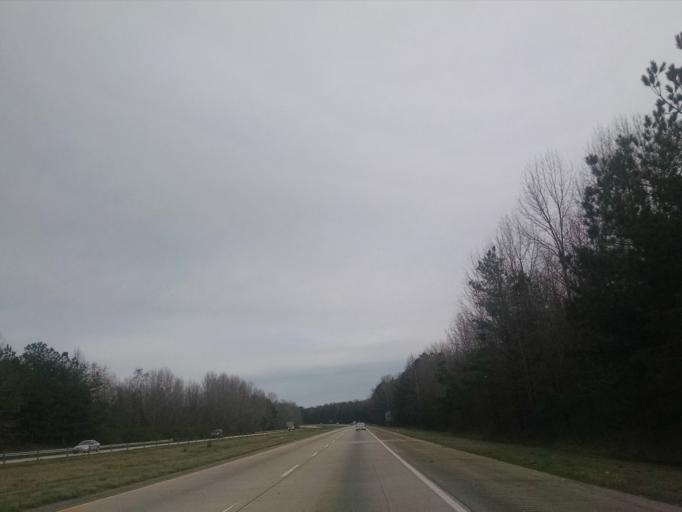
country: US
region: Georgia
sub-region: Hall County
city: Flowery Branch
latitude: 34.1514
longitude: -83.9358
